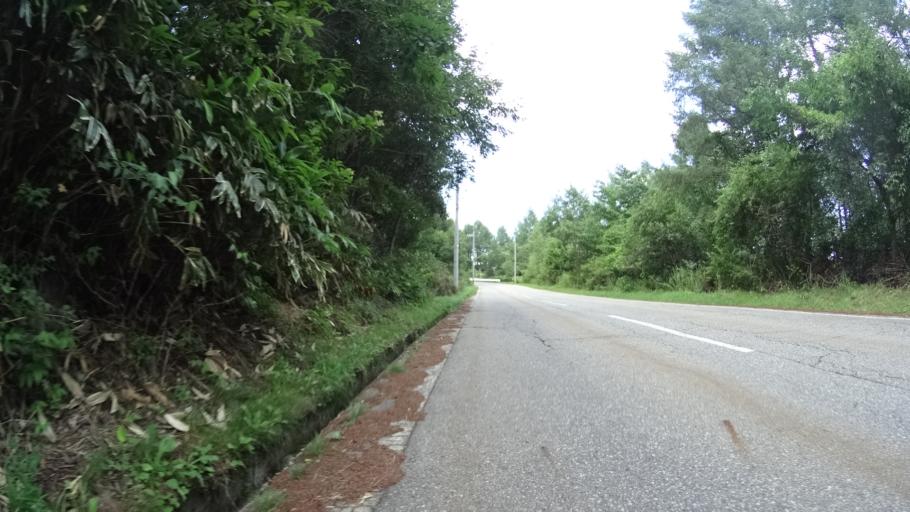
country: JP
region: Nagano
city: Saku
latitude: 36.0493
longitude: 138.4109
